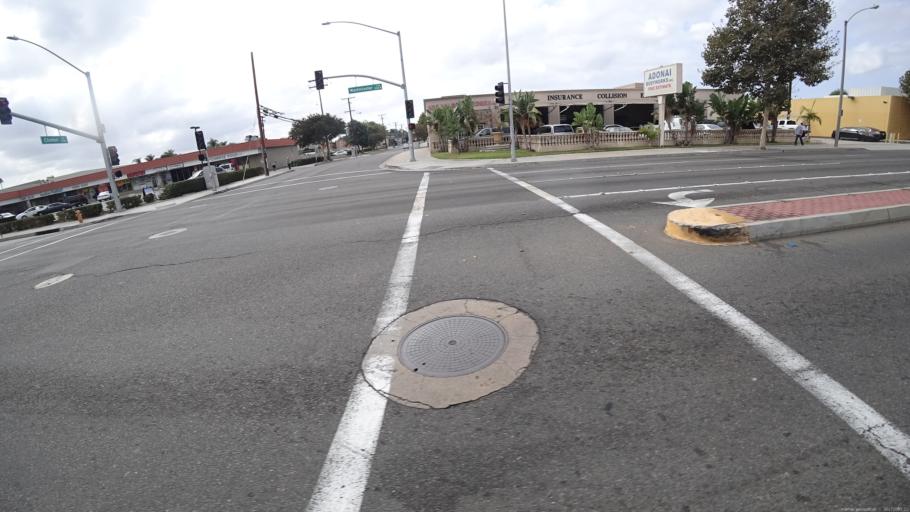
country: US
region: California
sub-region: Orange County
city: Garden Grove
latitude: 33.7599
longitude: -117.9116
